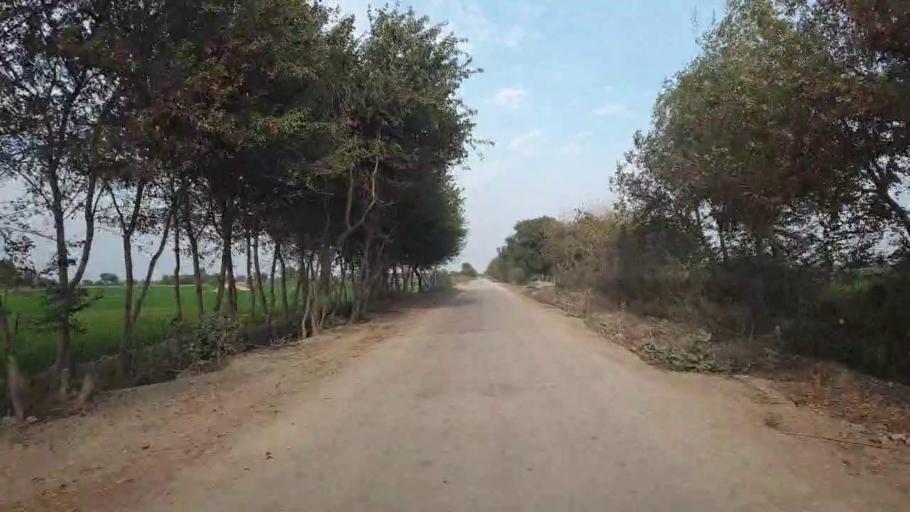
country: PK
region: Sindh
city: Shahdadpur
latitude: 26.0407
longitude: 68.5563
